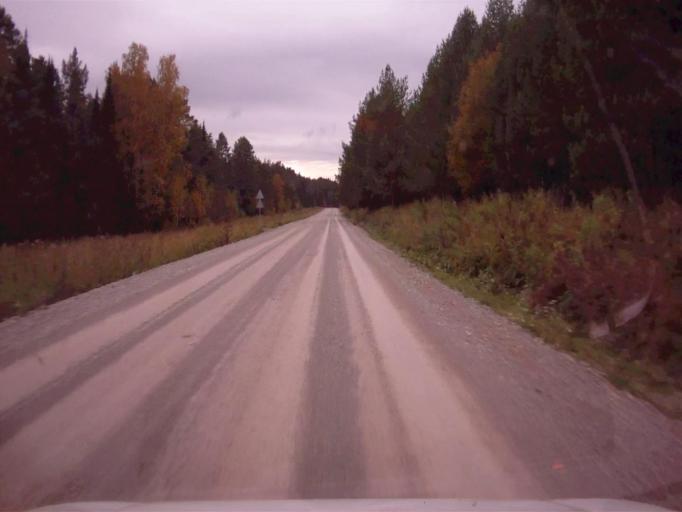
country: RU
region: Chelyabinsk
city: Nyazepetrovsk
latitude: 56.0476
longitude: 59.5255
